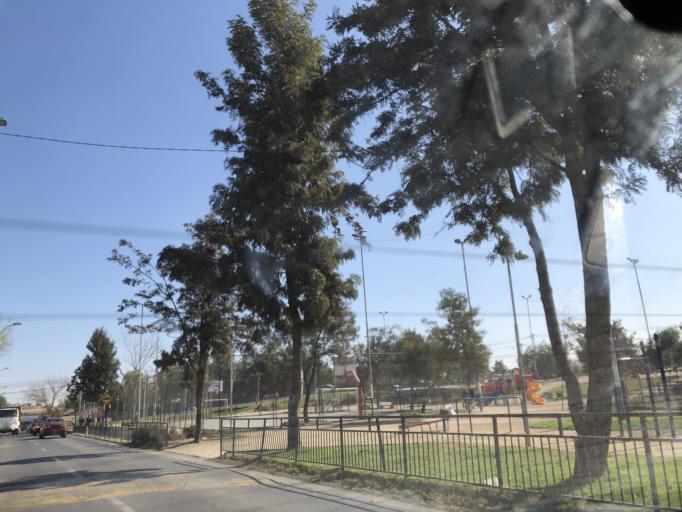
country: CL
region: Santiago Metropolitan
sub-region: Provincia de Cordillera
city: Puente Alto
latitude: -33.6195
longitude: -70.5961
